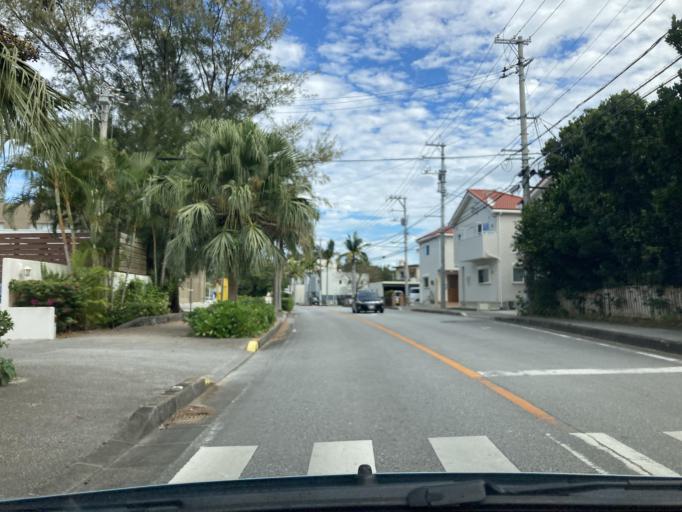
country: JP
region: Okinawa
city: Ishikawa
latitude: 26.4318
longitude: 127.7586
